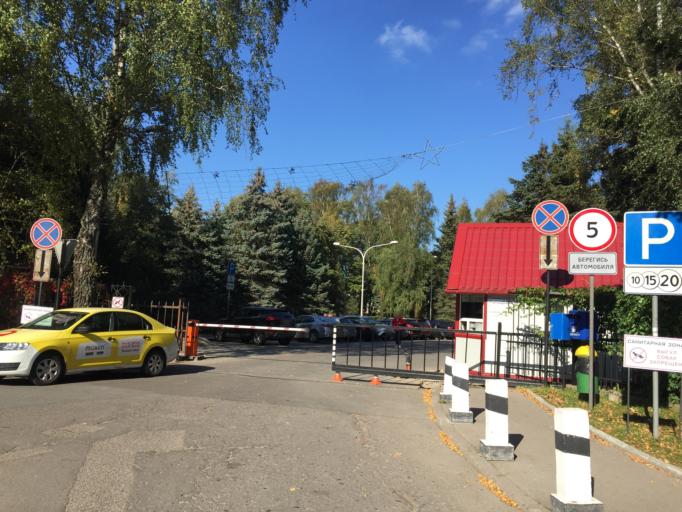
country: RU
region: Kaliningrad
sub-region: Gorod Svetlogorsk
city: Svetlogorsk
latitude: 54.9419
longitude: 20.1346
